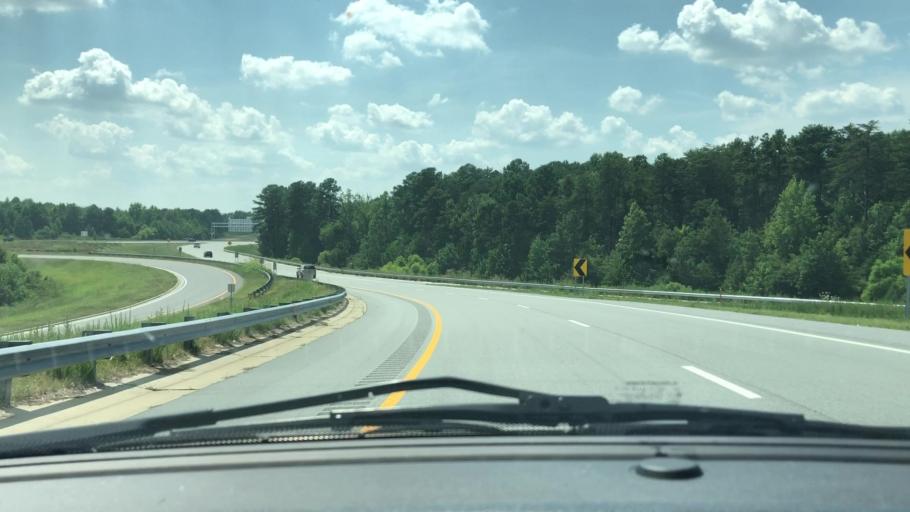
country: US
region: North Carolina
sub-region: Guilford County
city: Summerfield
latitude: 36.1190
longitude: -79.9076
